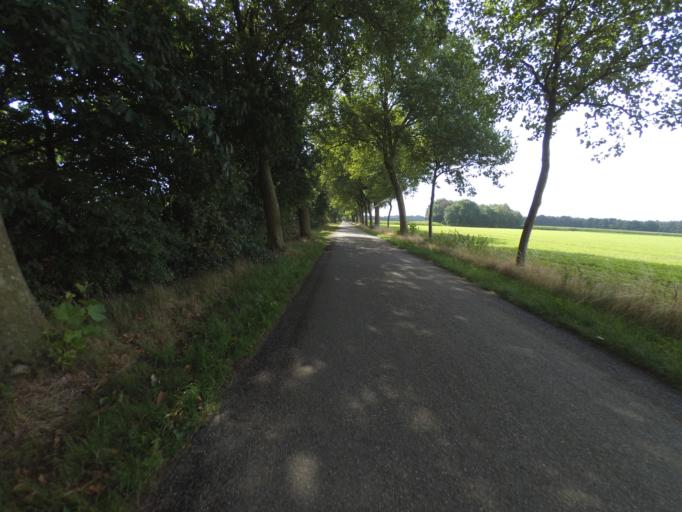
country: NL
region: Limburg
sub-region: Gemeente Echt-Susteren
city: Koningsbosch
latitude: 51.0638
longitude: 5.9363
